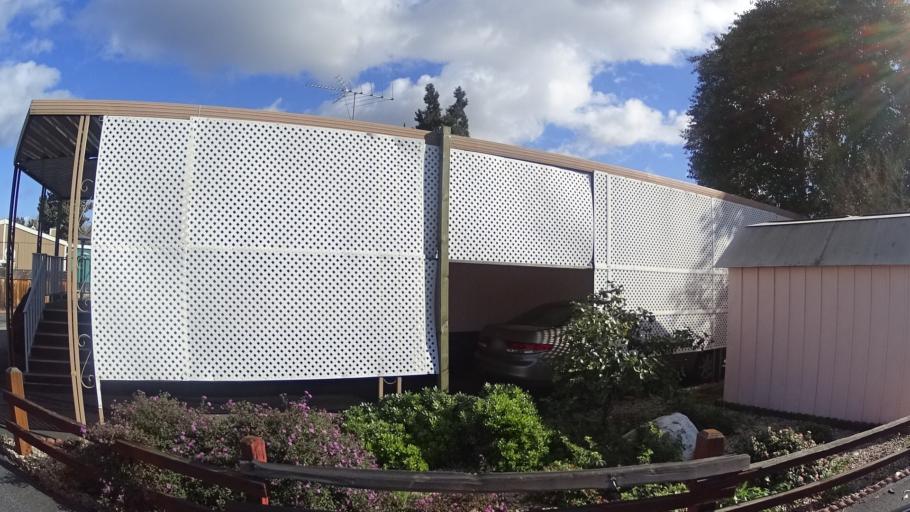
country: US
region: California
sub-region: Santa Clara County
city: Mountain View
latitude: 37.3820
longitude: -122.0658
